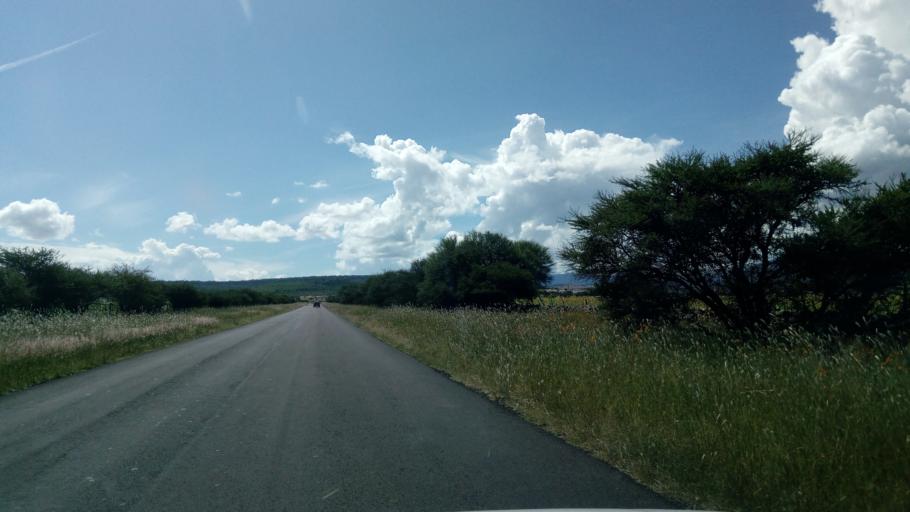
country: MX
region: Durango
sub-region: Durango
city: Jose Refugio Salcido
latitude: 23.8591
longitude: -104.4742
